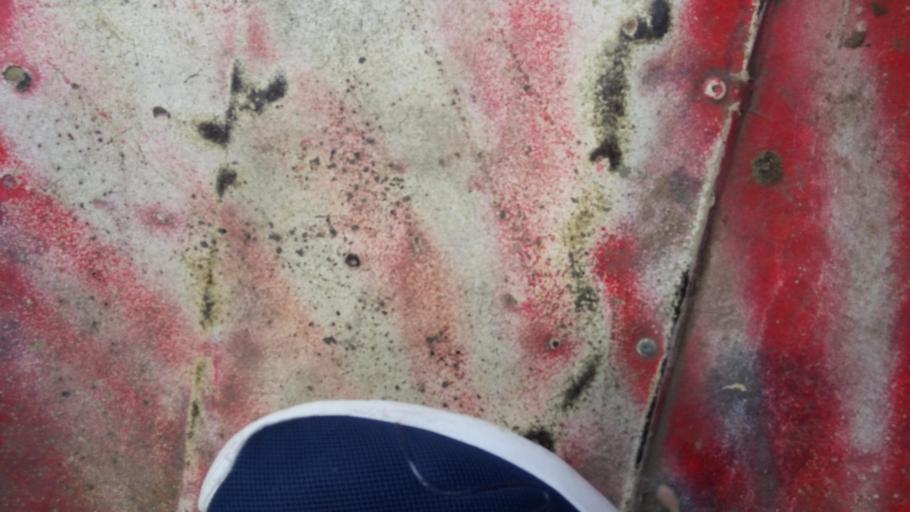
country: PH
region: Ilocos
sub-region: Province of La Union
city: Payocpoc Sur
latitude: 16.5029
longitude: 120.3325
